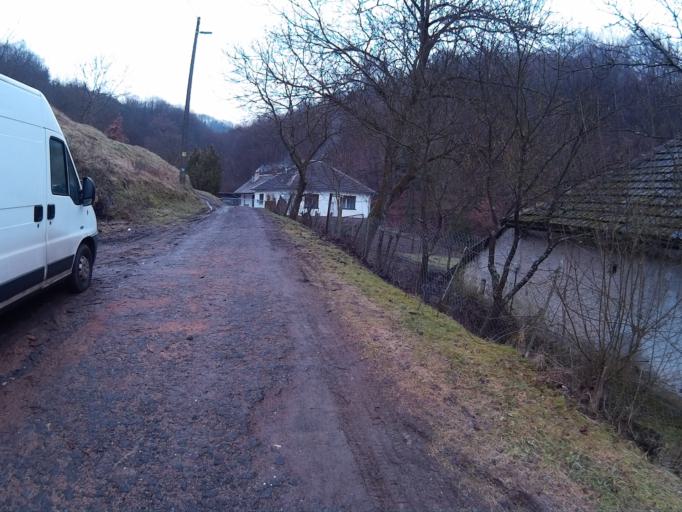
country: HU
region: Borsod-Abauj-Zemplen
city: Sarospatak
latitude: 48.4231
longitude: 21.5425
